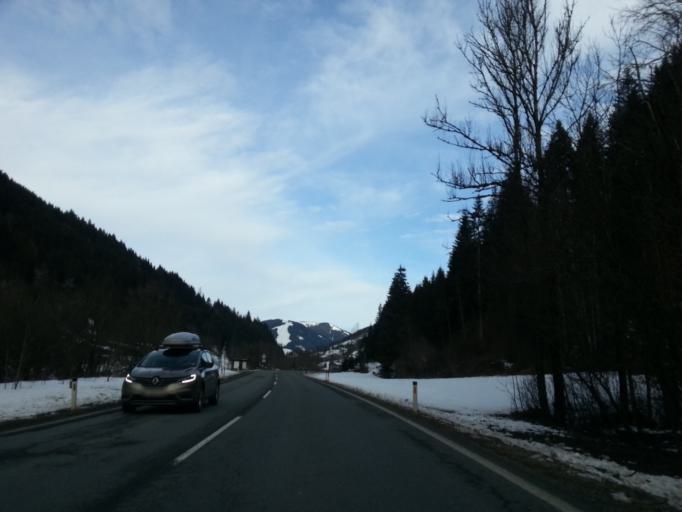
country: AT
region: Salzburg
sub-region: Politischer Bezirk Zell am See
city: Viehhofen
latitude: 47.3718
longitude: 12.6942
